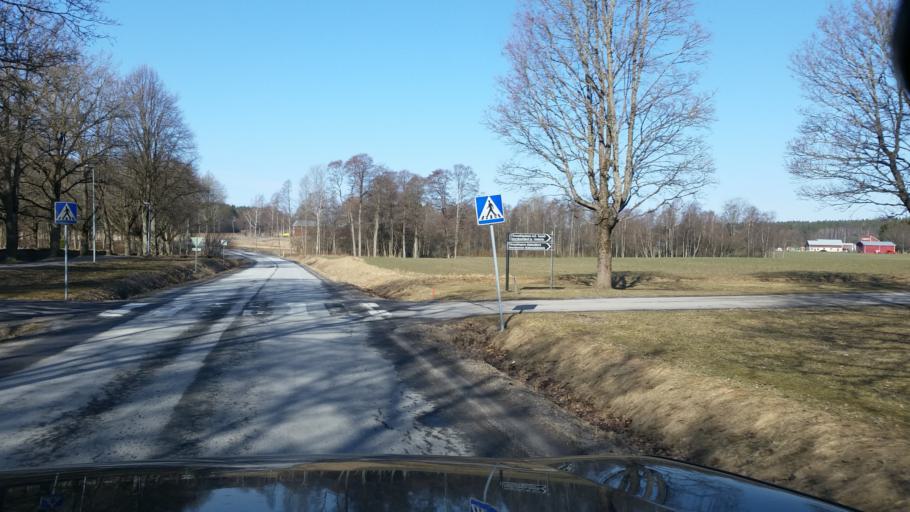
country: FI
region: Uusimaa
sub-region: Raaseporin
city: Inga
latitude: 60.0461
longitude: 24.0054
